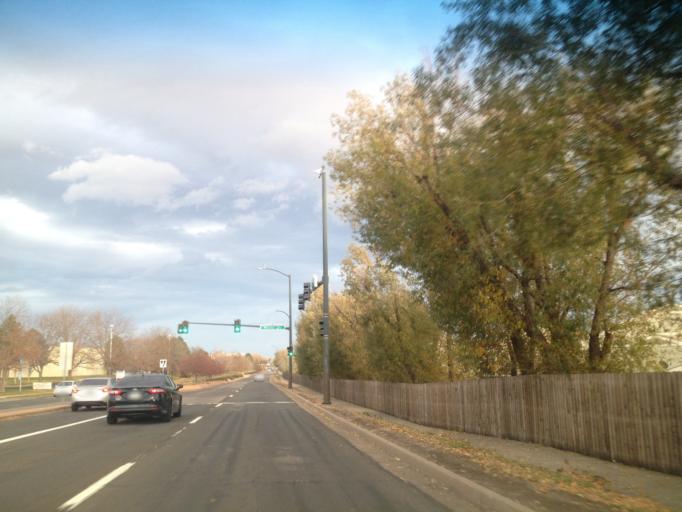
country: US
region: Colorado
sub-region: Adams County
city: Westminster
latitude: 39.8564
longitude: -105.0747
